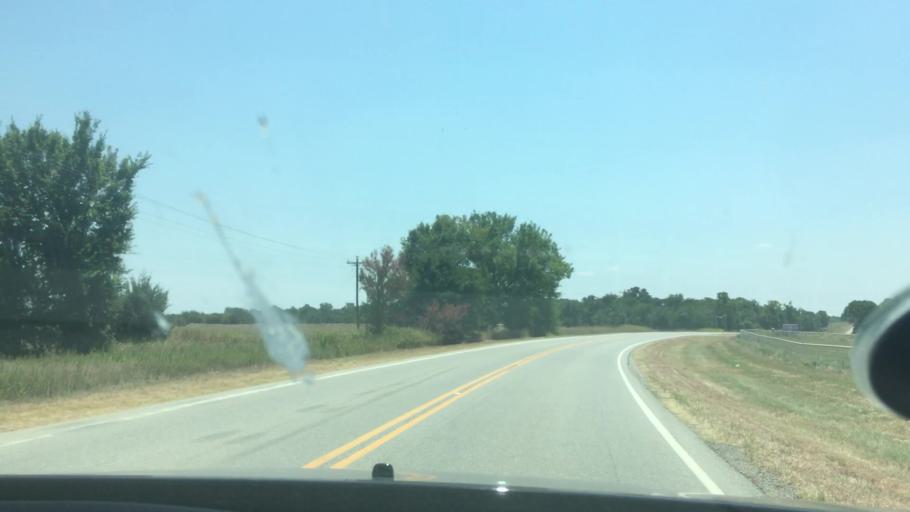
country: US
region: Oklahoma
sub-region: Coal County
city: Coalgate
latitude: 34.5779
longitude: -96.4073
